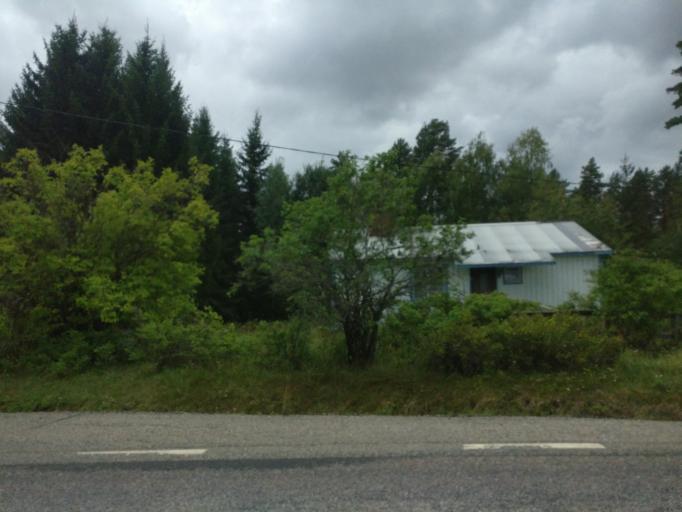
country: SE
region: Vaermland
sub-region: Torsby Kommun
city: Torsby
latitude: 60.7578
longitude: 12.7703
